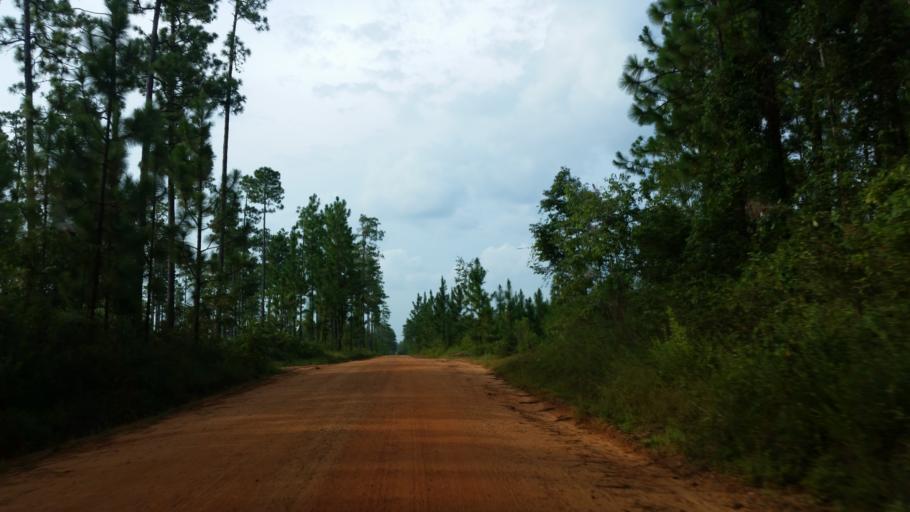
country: US
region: Alabama
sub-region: Escambia County
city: Atmore
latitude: 30.8718
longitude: -87.5825
